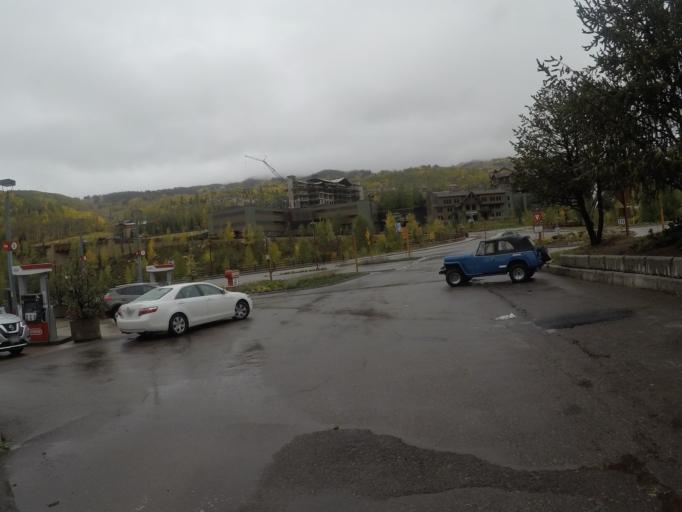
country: US
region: Colorado
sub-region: Pitkin County
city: Snowmass Village
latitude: 39.2107
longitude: -106.9469
